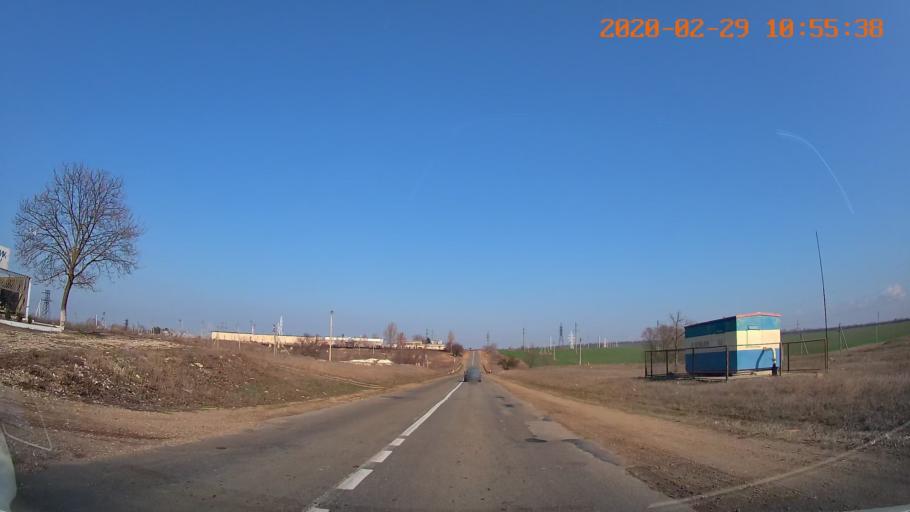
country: MD
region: Telenesti
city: Grigoriopol
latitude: 47.1360
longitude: 29.3253
